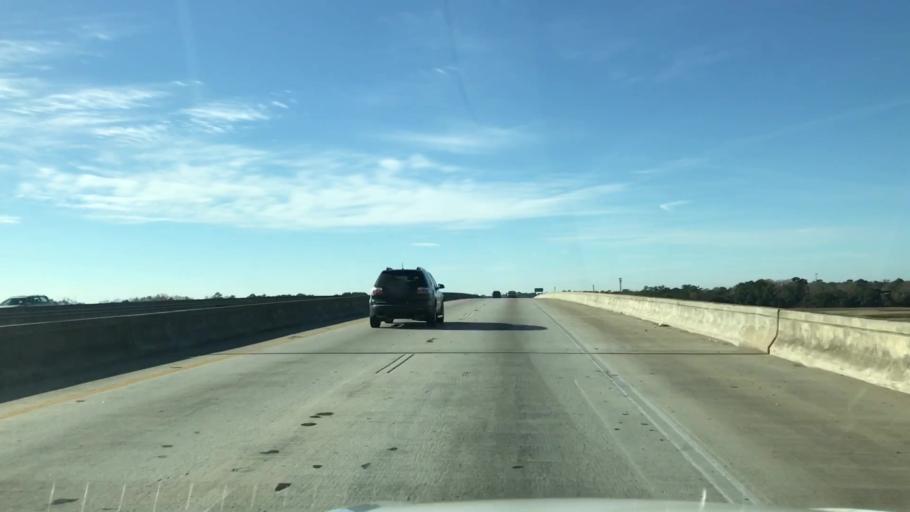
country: US
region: South Carolina
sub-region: Charleston County
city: North Charleston
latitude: 32.8356
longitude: -80.0245
